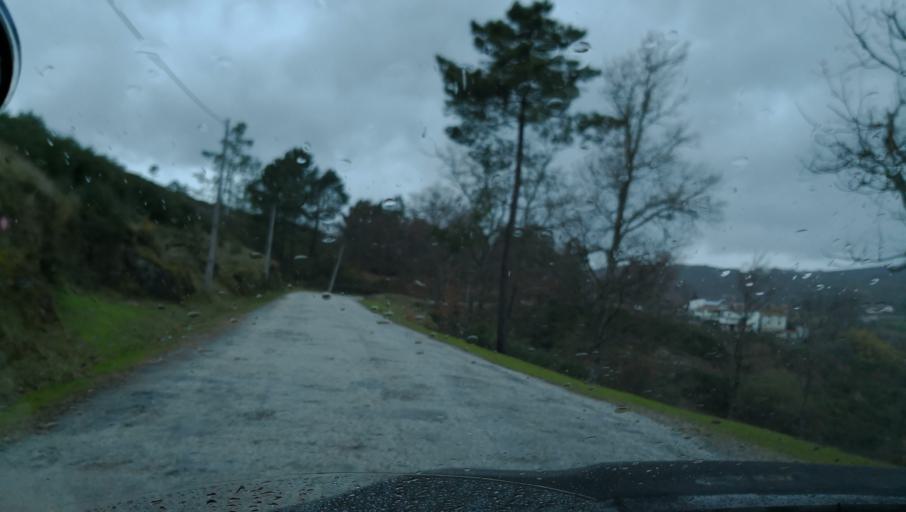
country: PT
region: Vila Real
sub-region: Vila Real
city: Vila Real
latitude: 41.2815
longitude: -7.7984
